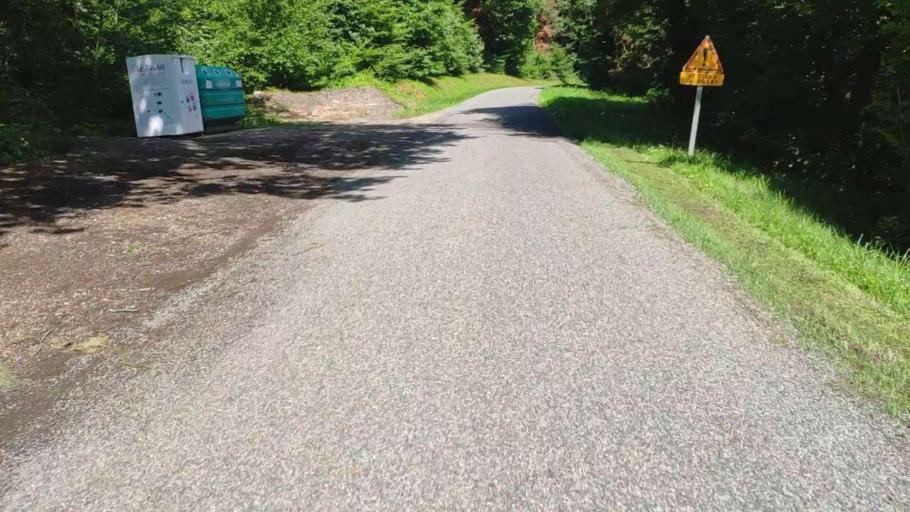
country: FR
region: Franche-Comte
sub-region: Departement du Jura
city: Bletterans
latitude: 46.8060
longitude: 5.5620
